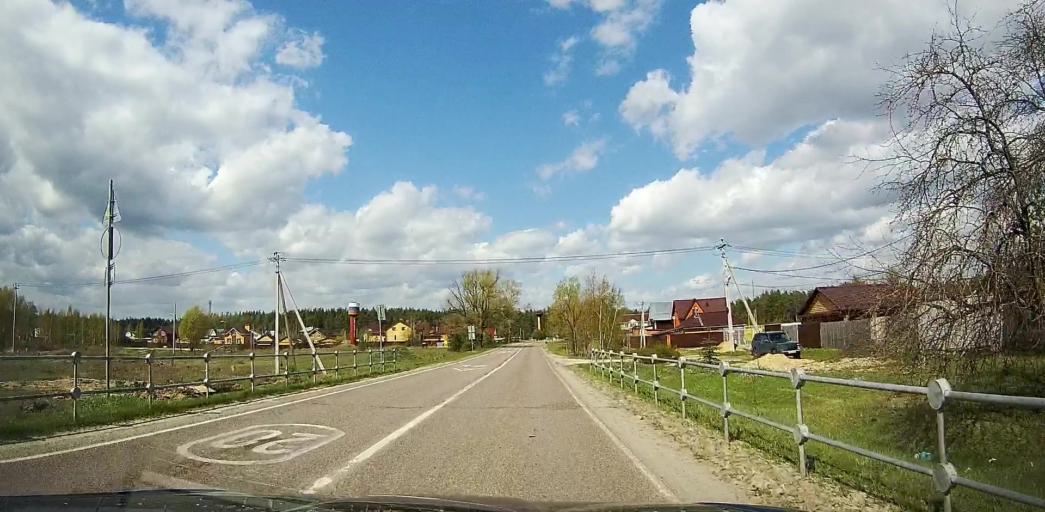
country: RU
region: Moskovskaya
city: Davydovo
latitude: 55.5591
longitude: 38.8132
